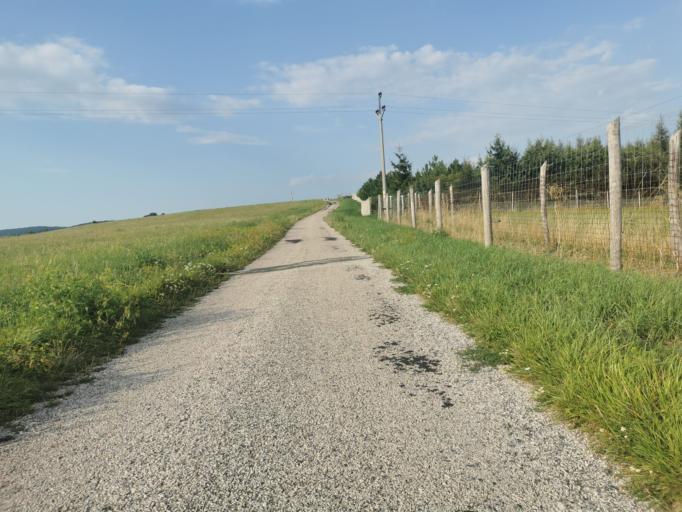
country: SK
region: Trenciansky
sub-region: Okres Myjava
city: Myjava
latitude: 48.7908
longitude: 17.5702
